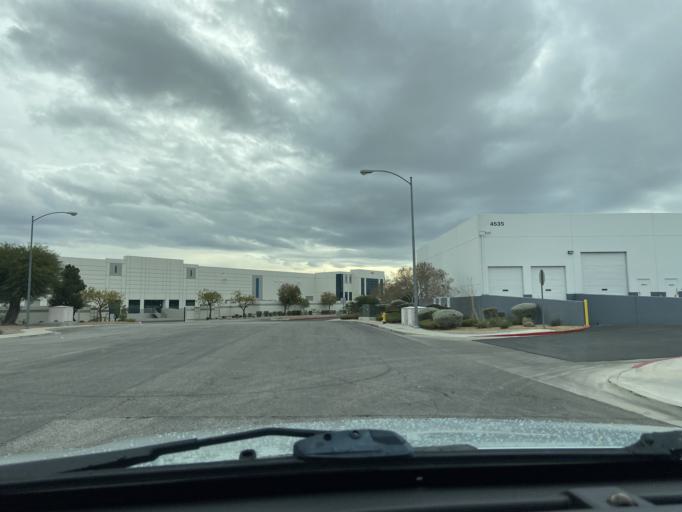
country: US
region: Nevada
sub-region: Clark County
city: North Las Vegas
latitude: 36.2425
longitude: -115.1078
